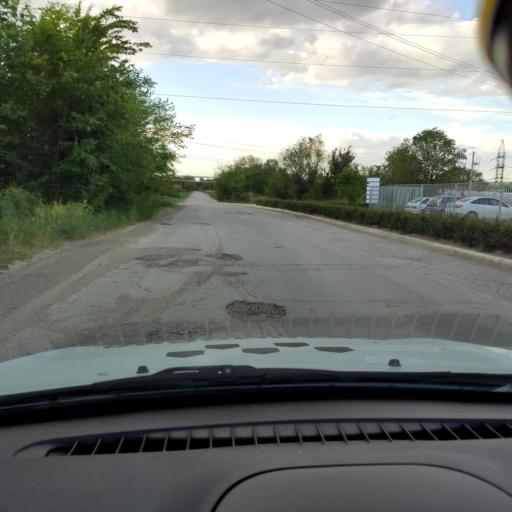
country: RU
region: Samara
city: Podstepki
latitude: 53.5794
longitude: 49.2286
